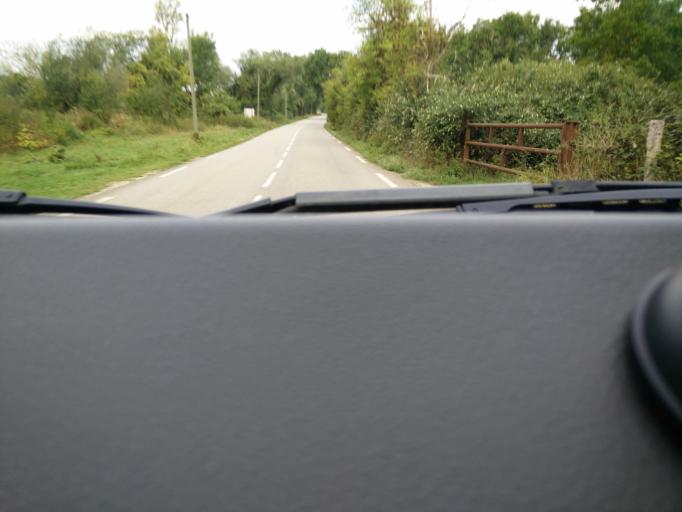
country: FR
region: Lorraine
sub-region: Departement de Meurthe-et-Moselle
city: Belleville
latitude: 48.8231
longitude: 6.1120
